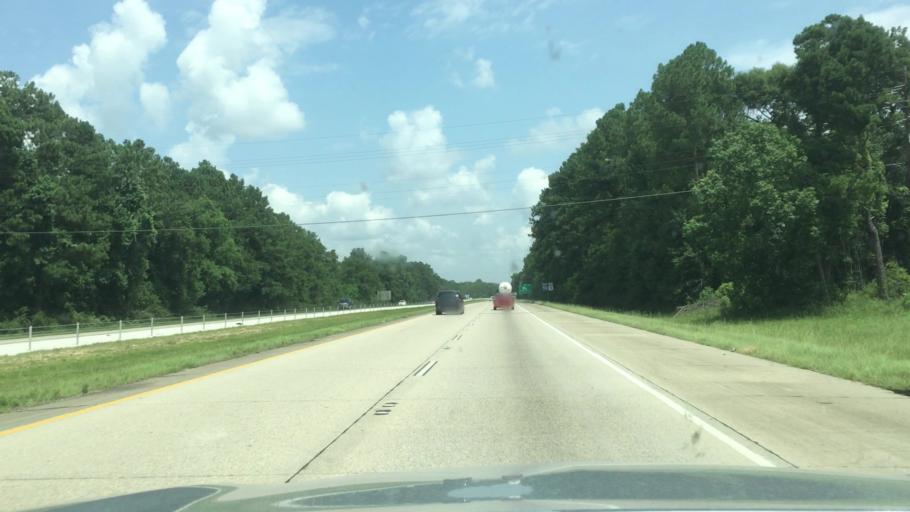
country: US
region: Louisiana
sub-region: Saint Tammany Parish
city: Pearl River
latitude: 30.3582
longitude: -89.7414
